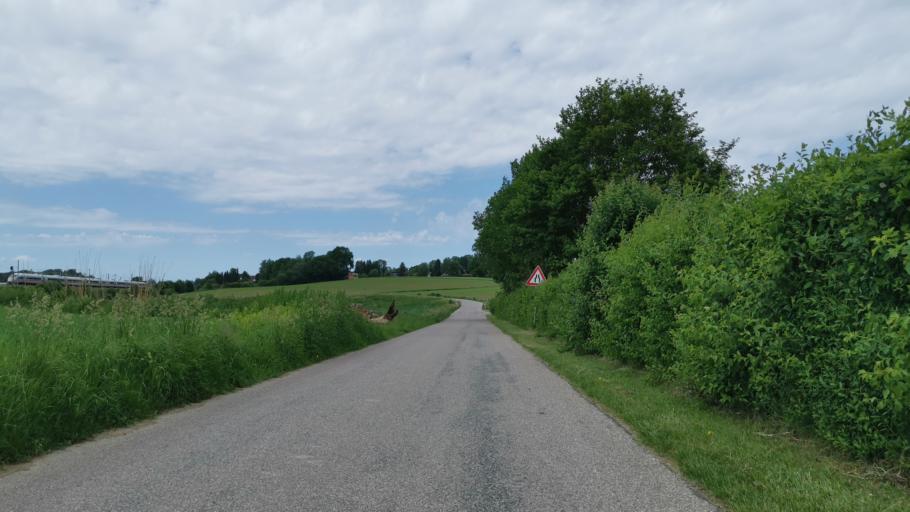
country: DE
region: Bavaria
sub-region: Upper Bavaria
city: Althegnenberg
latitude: 48.2402
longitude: 11.0551
